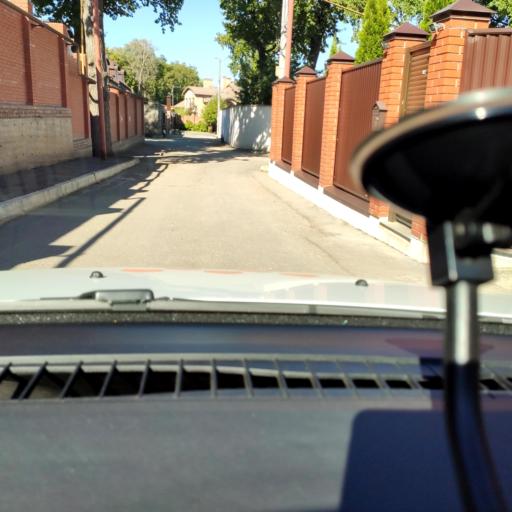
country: RU
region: Samara
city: Samara
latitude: 53.2639
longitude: 50.1903
